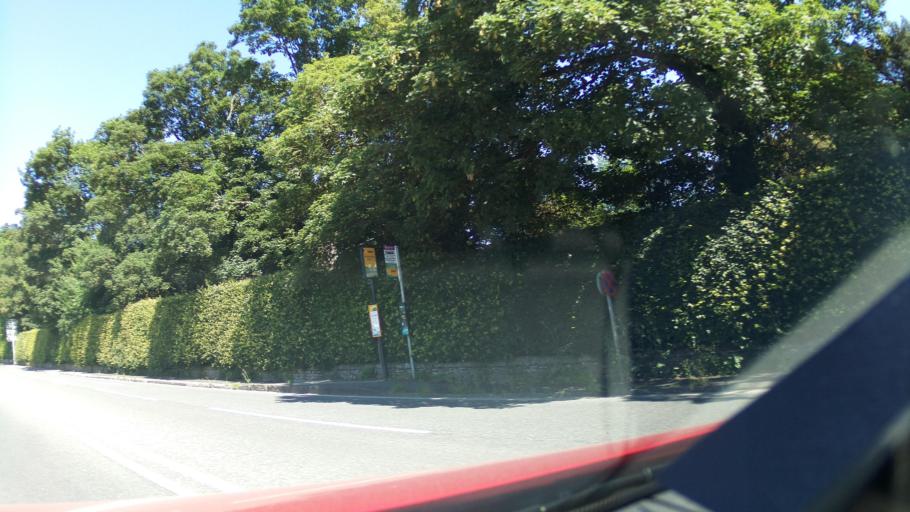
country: GB
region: England
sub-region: Derbyshire
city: Bakewell
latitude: 53.1917
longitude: -1.6510
